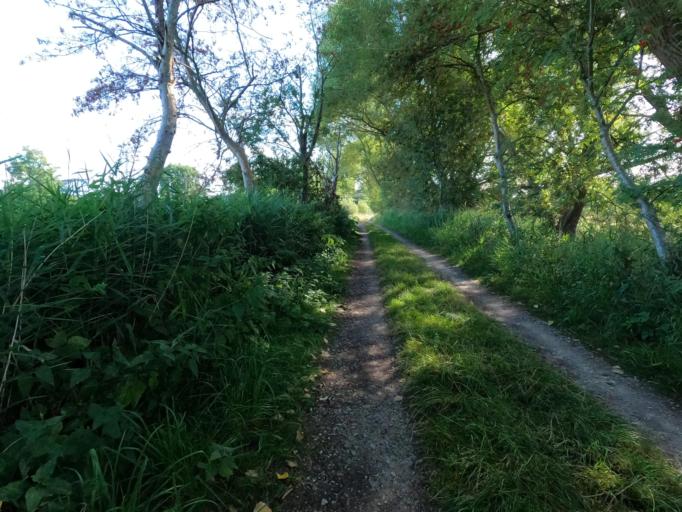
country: BE
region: Flanders
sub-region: Provincie Antwerpen
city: Grobbendonk
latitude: 51.1647
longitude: 4.7413
